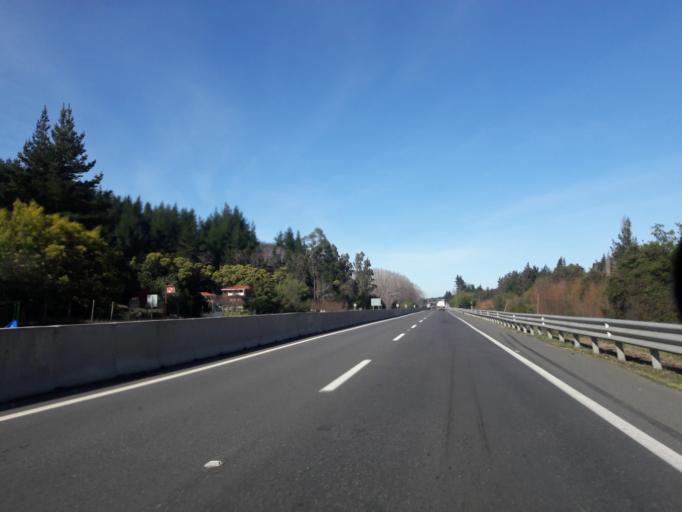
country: CL
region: Biobio
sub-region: Provincia de Biobio
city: Yumbel
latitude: -36.9431
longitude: -72.7556
